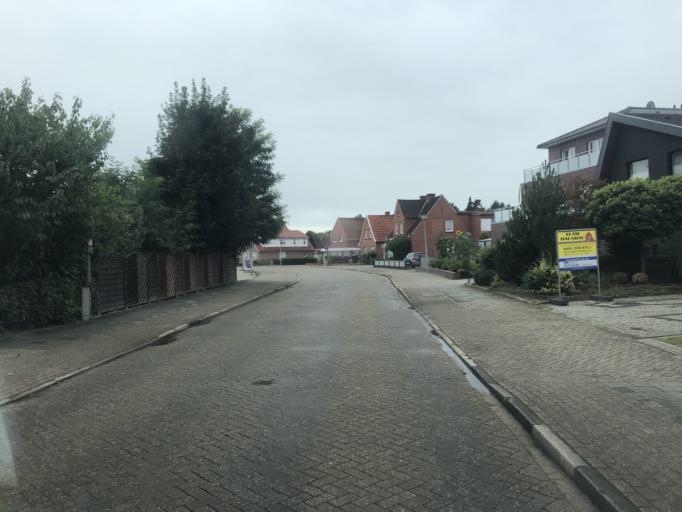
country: DE
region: Lower Saxony
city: Leer
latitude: 53.2431
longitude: 7.4588
